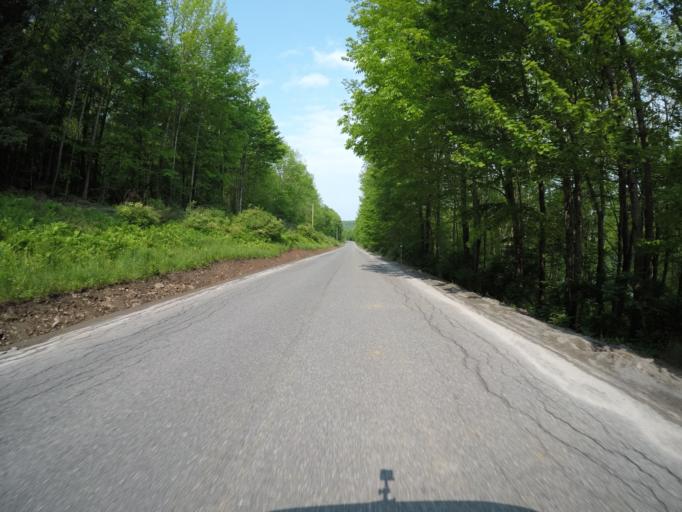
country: US
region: New York
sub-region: Sullivan County
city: Livingston Manor
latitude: 42.1126
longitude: -74.7580
